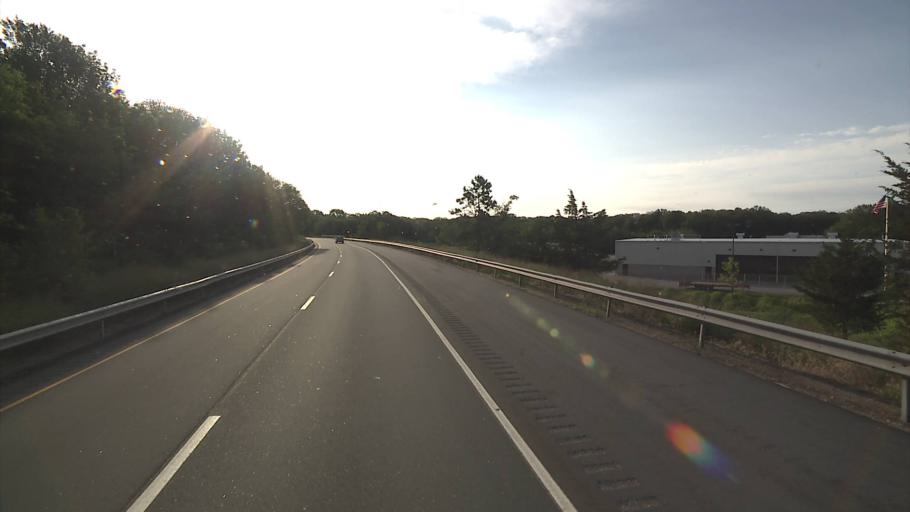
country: US
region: Connecticut
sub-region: New London County
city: Colchester
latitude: 41.5619
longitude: -72.3224
